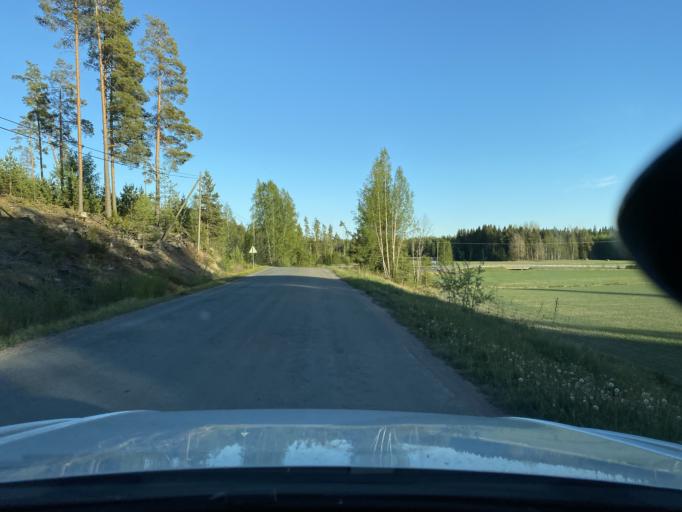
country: FI
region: Satakunta
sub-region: Rauma
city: Kiukainen
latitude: 61.1325
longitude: 21.9880
